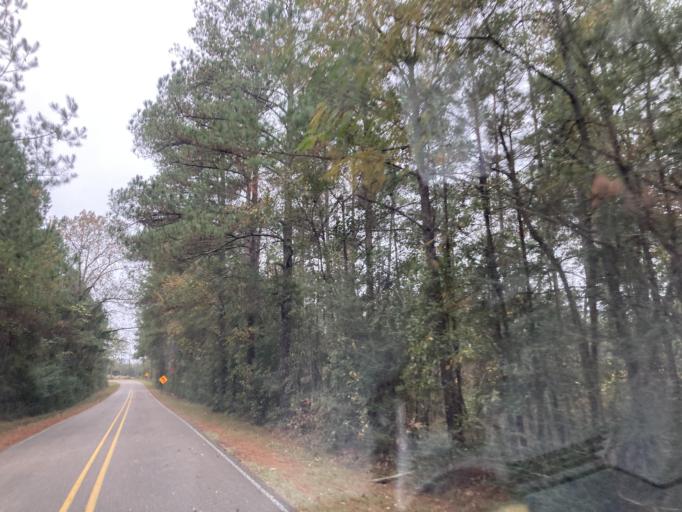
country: US
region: Mississippi
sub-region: Lamar County
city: Purvis
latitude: 31.0804
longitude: -89.3503
